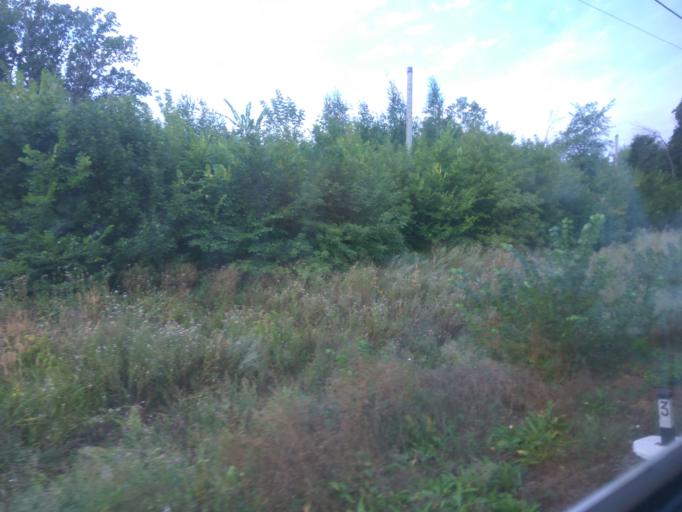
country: RU
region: Saratov
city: Rtishchevo
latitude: 52.2231
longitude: 43.8614
